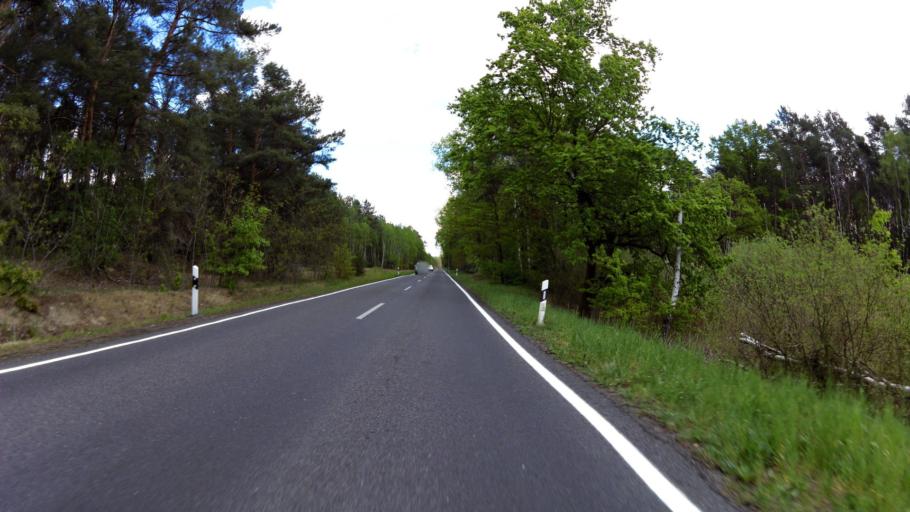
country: DE
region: Brandenburg
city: Schlepzig
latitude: 52.1037
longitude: 13.9187
